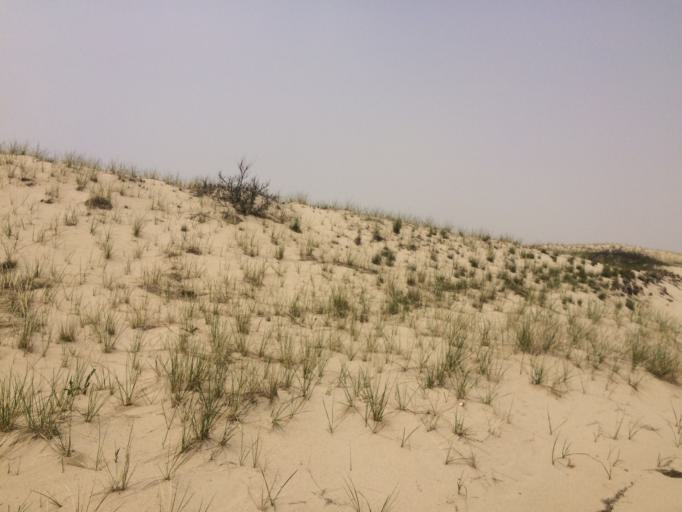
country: US
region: Massachusetts
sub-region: Barnstable County
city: Provincetown
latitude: 42.0706
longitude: -70.2362
